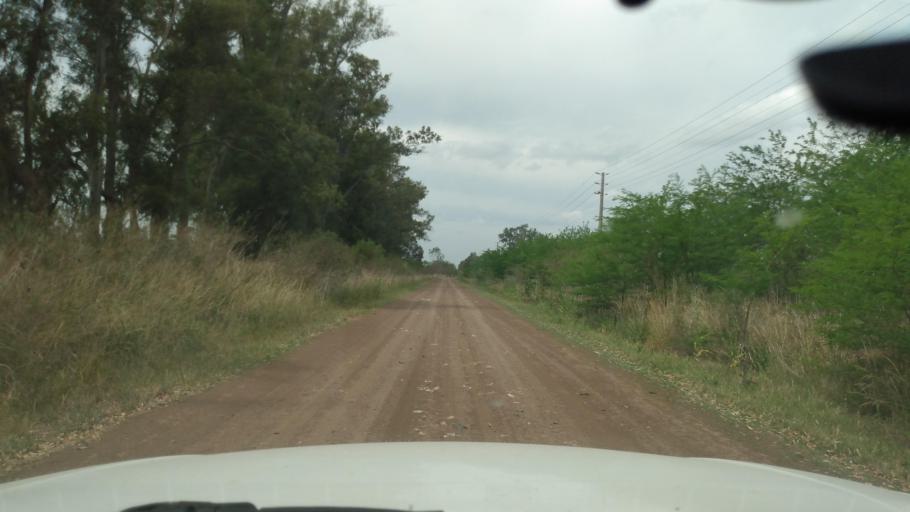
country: AR
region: Buenos Aires
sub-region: Partido de Lujan
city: Lujan
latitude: -34.5525
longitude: -59.1721
